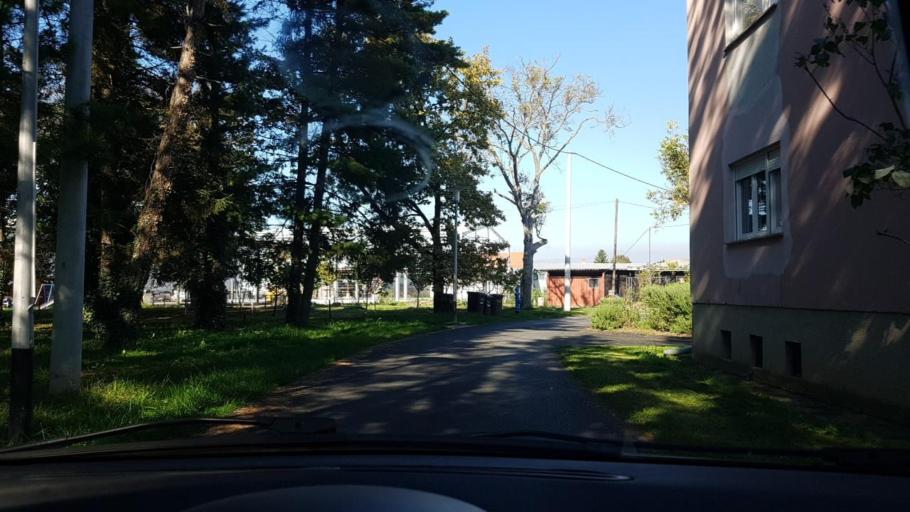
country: HR
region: Grad Zagreb
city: Lucko
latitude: 45.7588
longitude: 15.8856
